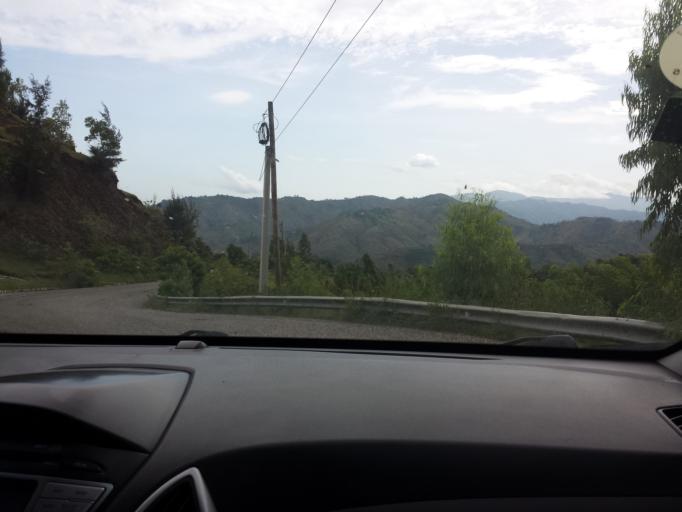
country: HT
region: Ouest
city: Leogane
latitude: 18.3947
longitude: -72.6237
